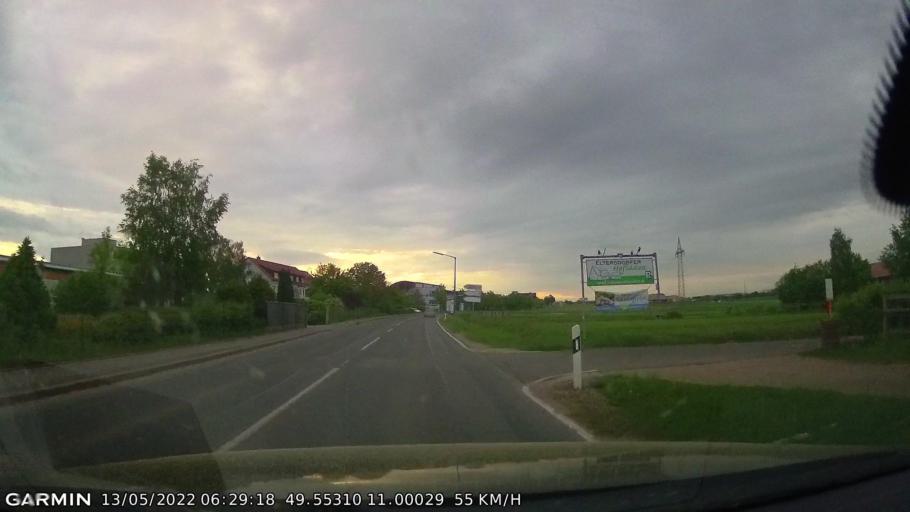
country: DE
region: Bavaria
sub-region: Regierungsbezirk Mittelfranken
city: Erlangen
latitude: 49.5530
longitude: 11.0004
